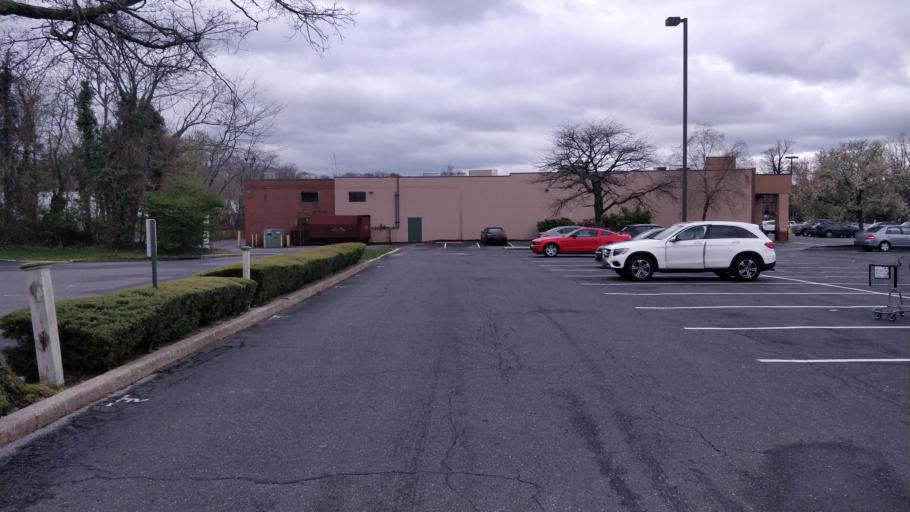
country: US
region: New York
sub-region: Suffolk County
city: East Setauket
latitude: 40.9385
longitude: -73.1086
